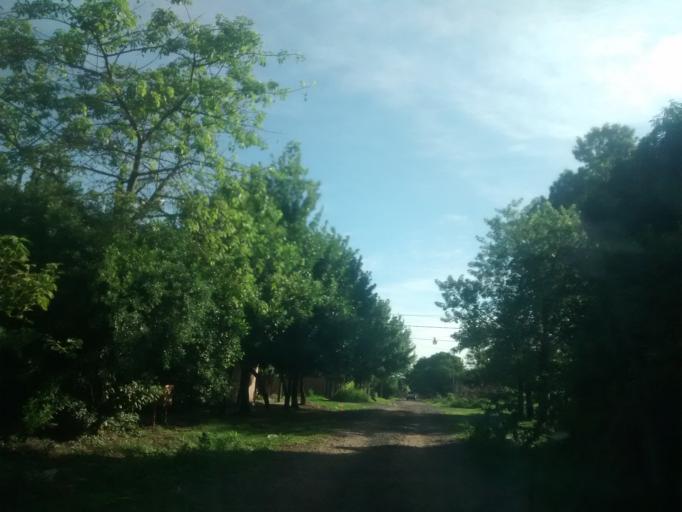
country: AR
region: Chaco
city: Puerto Tirol
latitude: -27.3764
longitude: -59.0944
